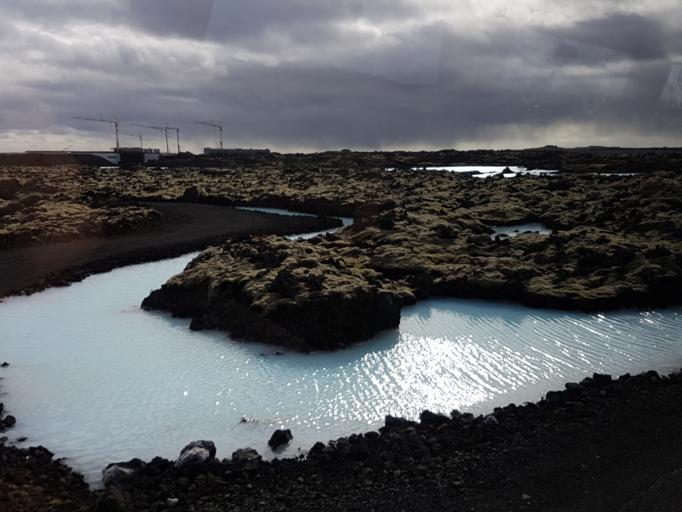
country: IS
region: Southern Peninsula
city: Grindavik
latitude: 63.8833
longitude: -22.4446
